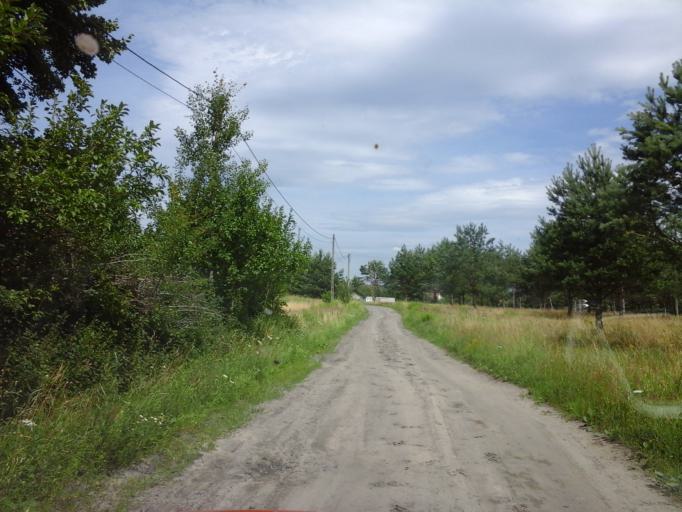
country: PL
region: Lubusz
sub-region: Powiat strzelecko-drezdenecki
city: Dobiegniew
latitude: 53.0811
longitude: 15.7917
